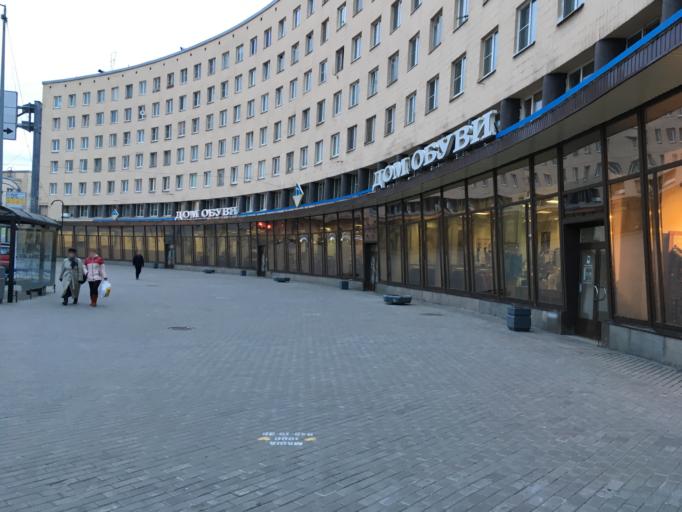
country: RU
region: St.-Petersburg
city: Centralniy
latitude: 59.9429
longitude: 30.4137
